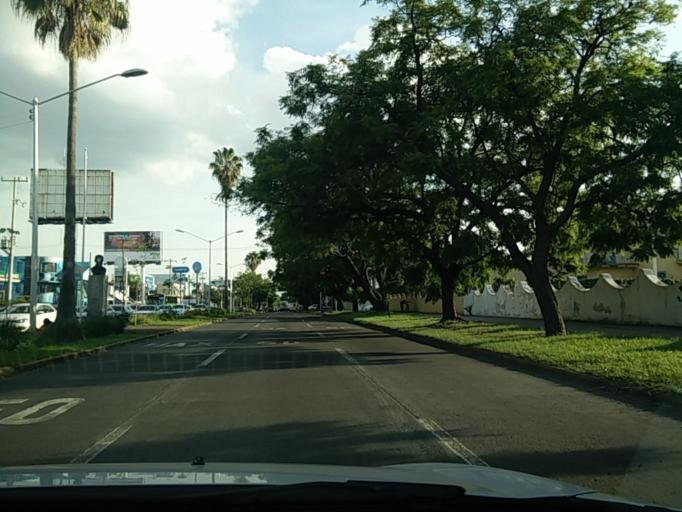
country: MX
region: Jalisco
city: Guadalajara
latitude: 20.6891
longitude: -103.3735
